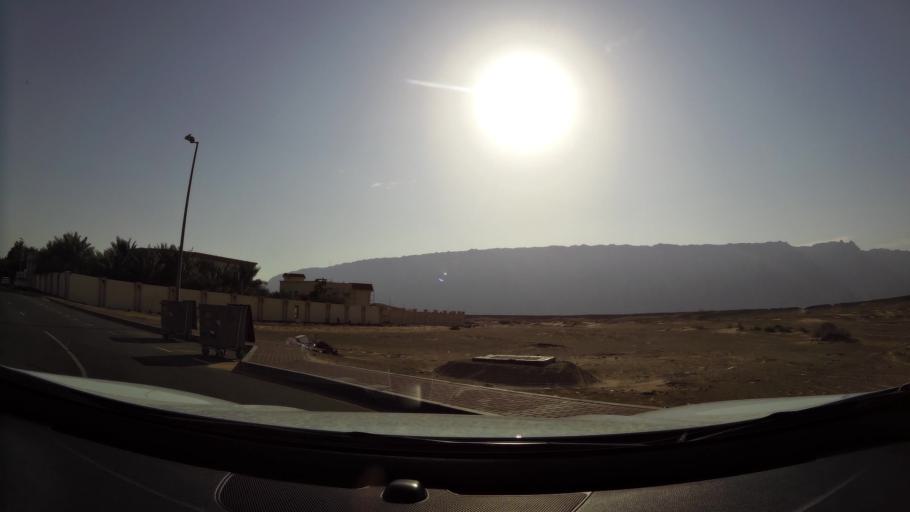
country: AE
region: Abu Dhabi
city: Al Ain
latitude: 24.0425
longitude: 55.8396
